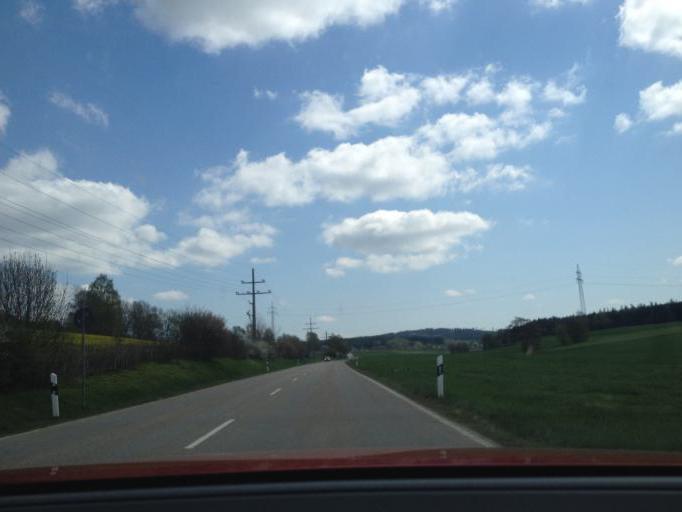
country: DE
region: Bavaria
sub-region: Upper Palatinate
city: Waldershof
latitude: 49.9836
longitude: 12.0781
